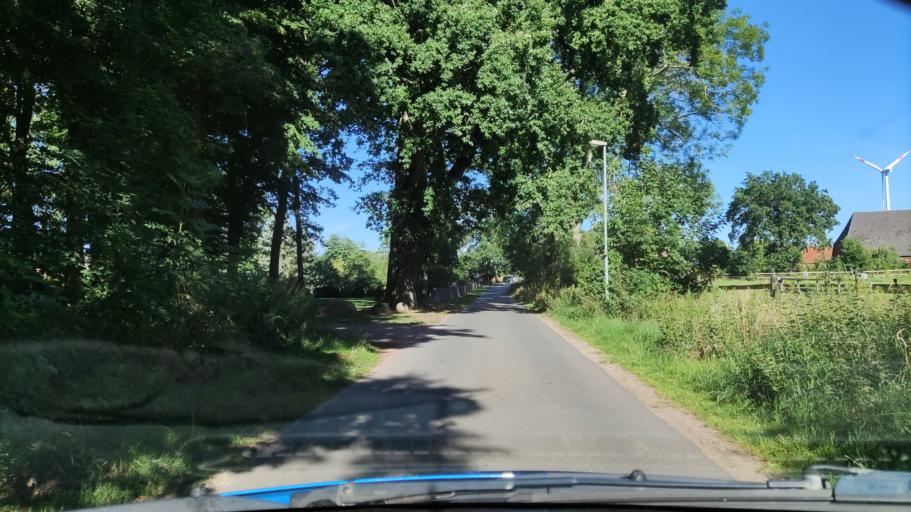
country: DE
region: Lower Saxony
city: Nahrendorf
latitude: 53.1804
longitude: 10.7821
